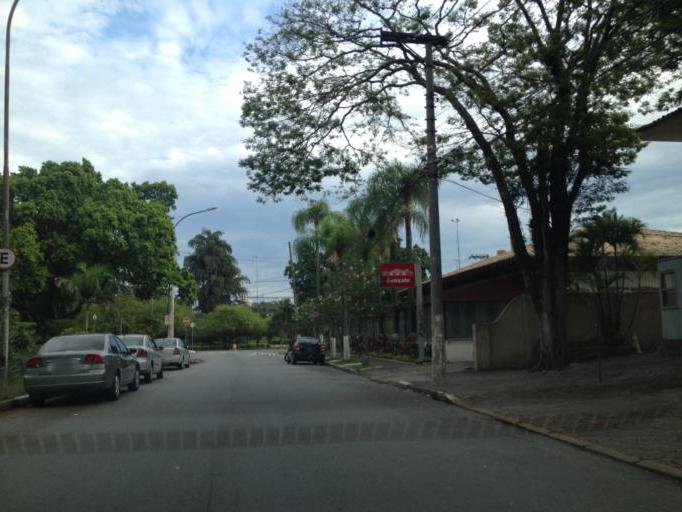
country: BR
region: Sao Paulo
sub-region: Sao Paulo
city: Sao Paulo
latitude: -23.5552
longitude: -46.7081
